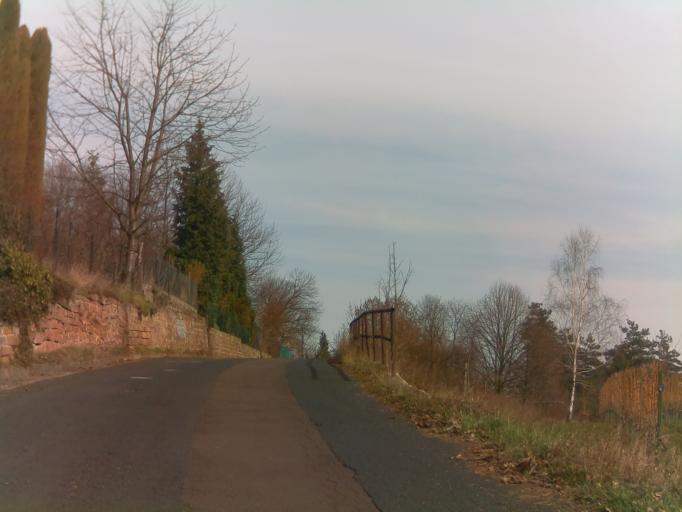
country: DE
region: Rheinland-Pfalz
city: Sankt Martin
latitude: 49.3015
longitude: 8.0932
